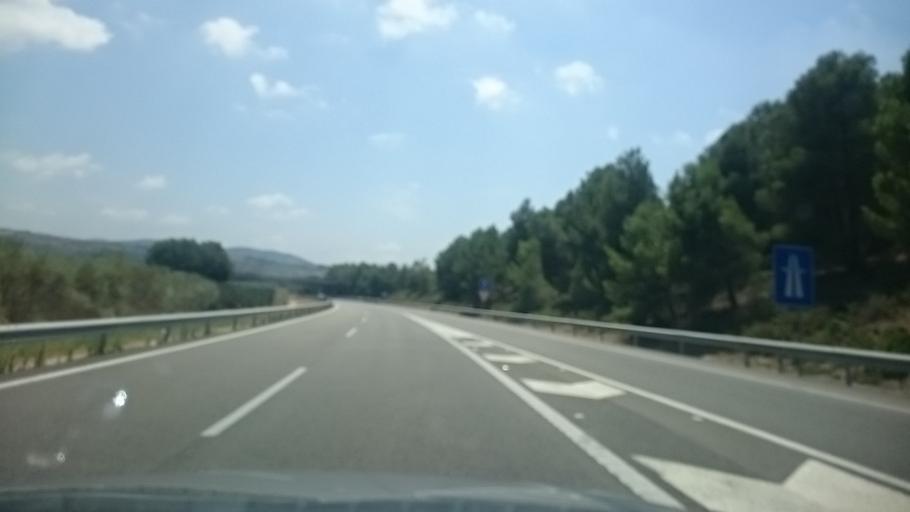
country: ES
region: Catalonia
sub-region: Provincia de Tarragona
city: Montferri
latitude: 41.2973
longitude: 1.3493
